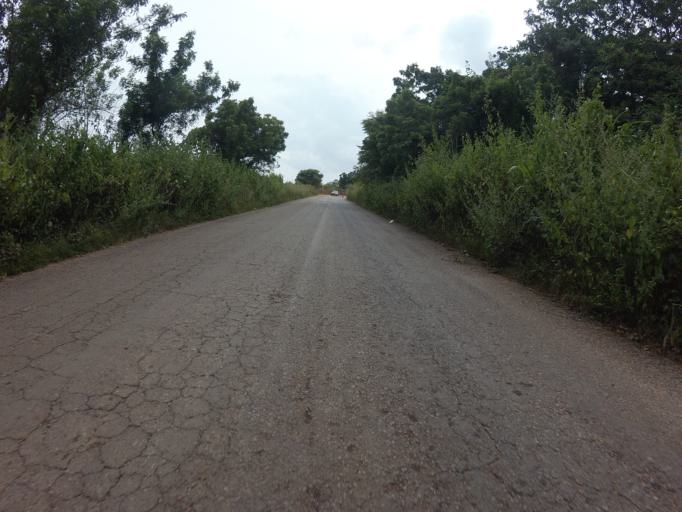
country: GH
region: Volta
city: Ho
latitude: 6.6746
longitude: 0.3523
